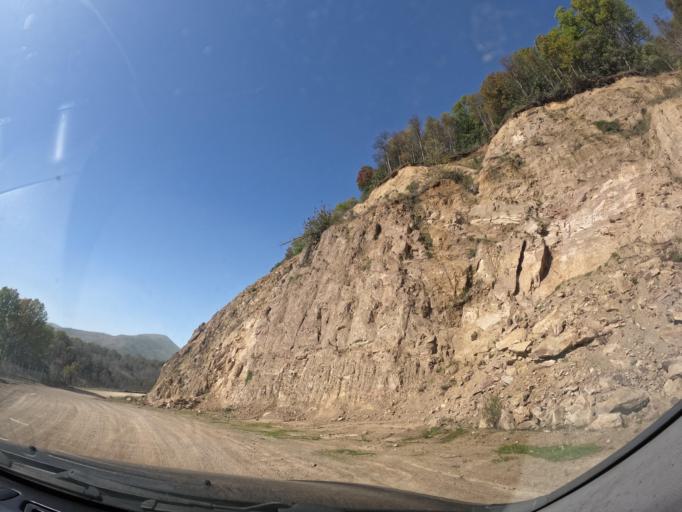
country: CL
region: Maule
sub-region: Provincia de Linares
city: Longavi
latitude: -36.2430
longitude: -71.4370
